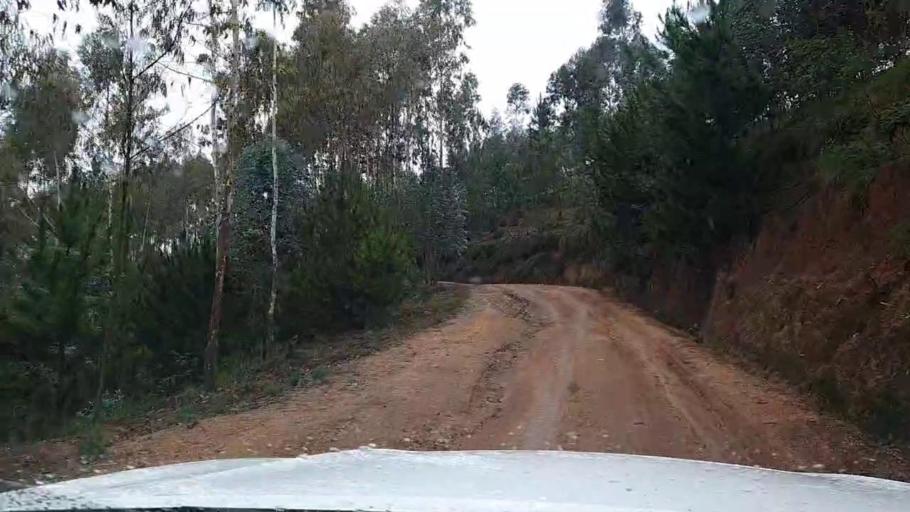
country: RW
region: Southern Province
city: Nzega
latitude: -2.4684
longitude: 29.4985
